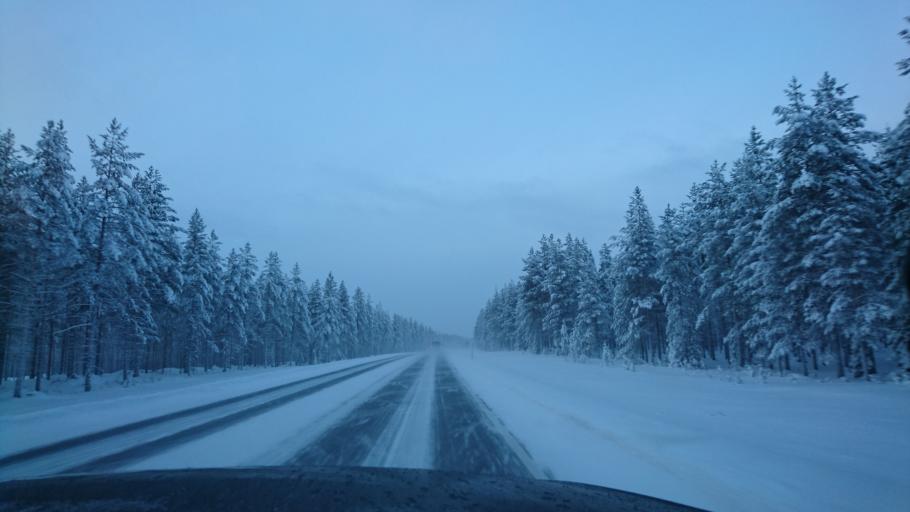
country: FI
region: Kainuu
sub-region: Kehys-Kainuu
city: Puolanka
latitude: 65.4307
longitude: 27.5594
